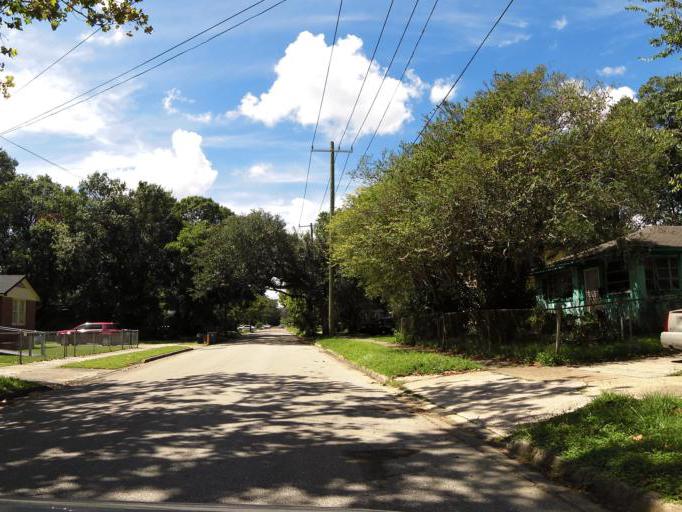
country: US
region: Florida
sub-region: Duval County
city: Jacksonville
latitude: 30.3567
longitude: -81.6785
